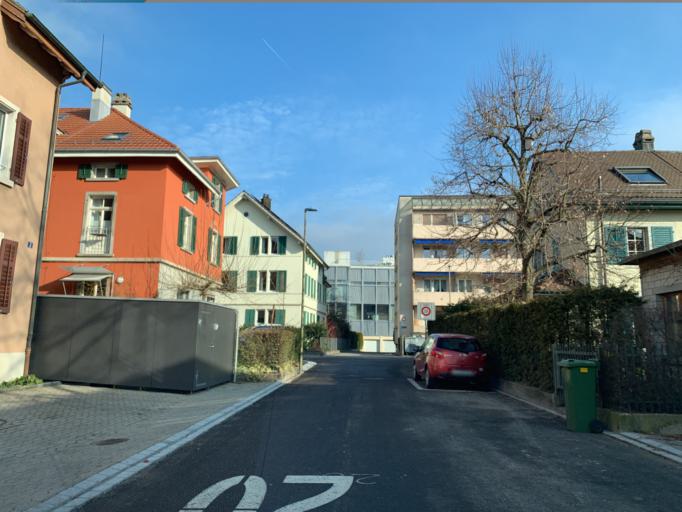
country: CH
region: Zurich
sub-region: Bezirk Winterthur
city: Toess (Kreis 4) / Eichliacker
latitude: 47.4914
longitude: 8.7093
